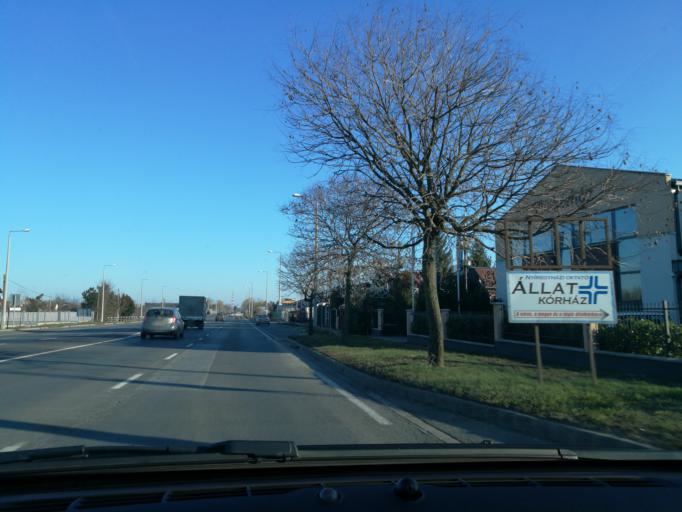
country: HU
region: Szabolcs-Szatmar-Bereg
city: Nyirpazony
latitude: 47.9506
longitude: 21.7678
